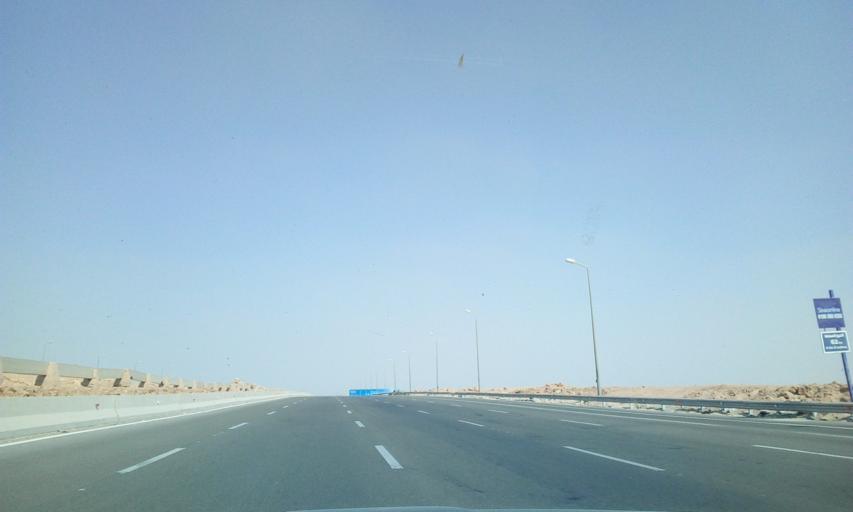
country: EG
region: Muhafazat al Qahirah
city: Halwan
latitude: 29.9011
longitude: 31.7884
